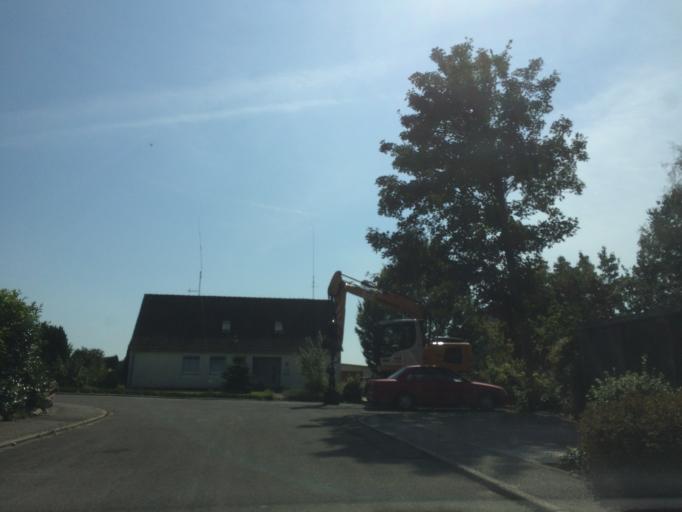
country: DE
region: Schleswig-Holstein
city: Holtsee
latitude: 54.4015
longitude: 9.8568
